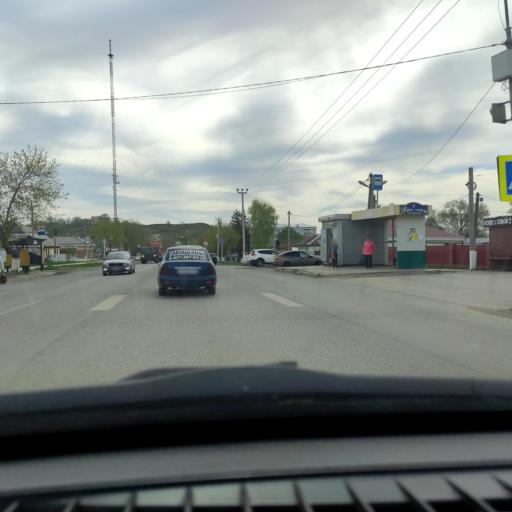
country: RU
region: Samara
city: Surgut
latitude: 53.9414
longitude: 51.1669
